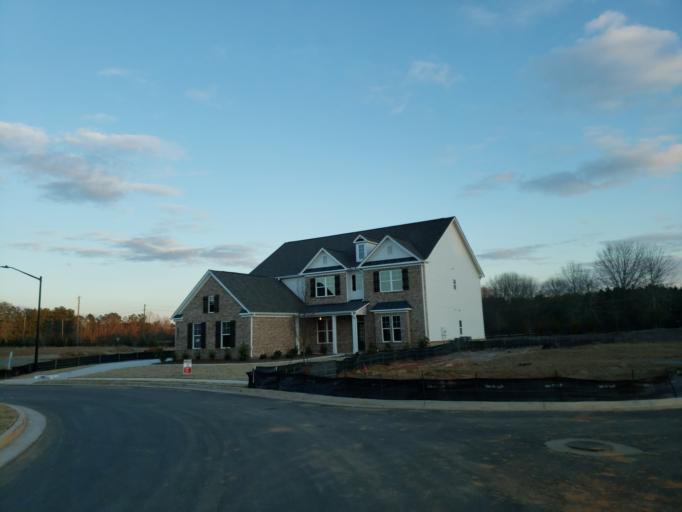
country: US
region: Georgia
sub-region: Cobb County
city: Acworth
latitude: 33.9751
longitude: -84.7169
